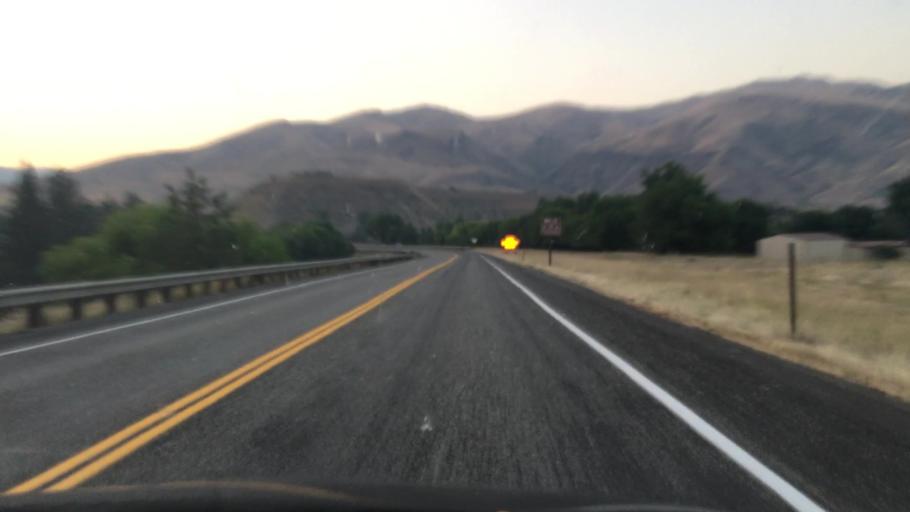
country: US
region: Idaho
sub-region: Idaho County
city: Grangeville
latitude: 45.6586
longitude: -116.2909
